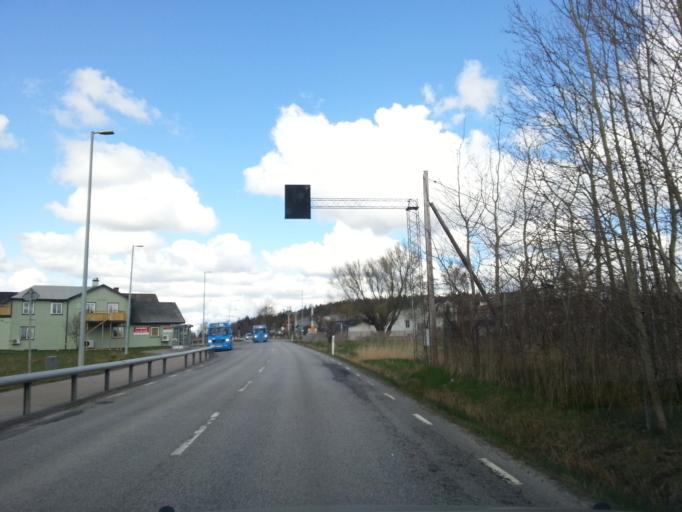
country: SE
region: Vaestra Goetaland
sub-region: Kungalvs Kommun
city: Kungalv
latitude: 57.8007
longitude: 11.9123
